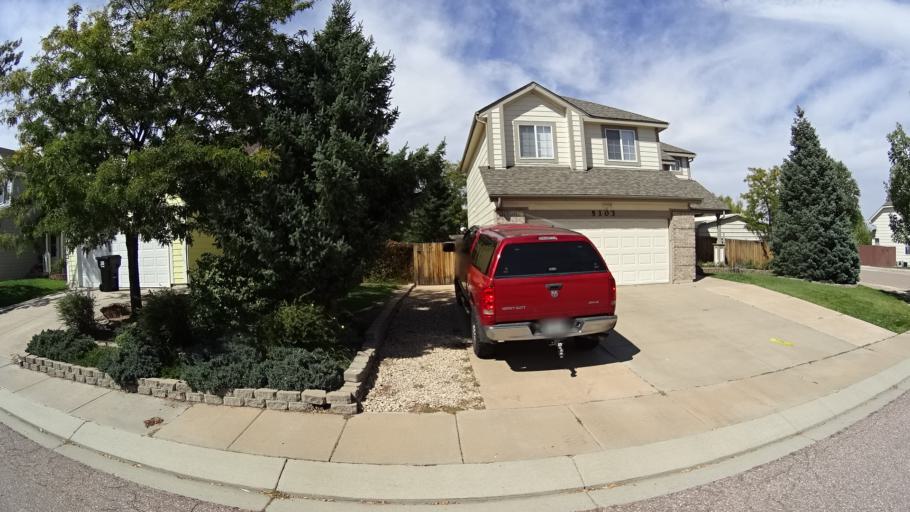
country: US
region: Colorado
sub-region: El Paso County
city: Cimarron Hills
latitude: 38.9037
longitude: -104.7126
